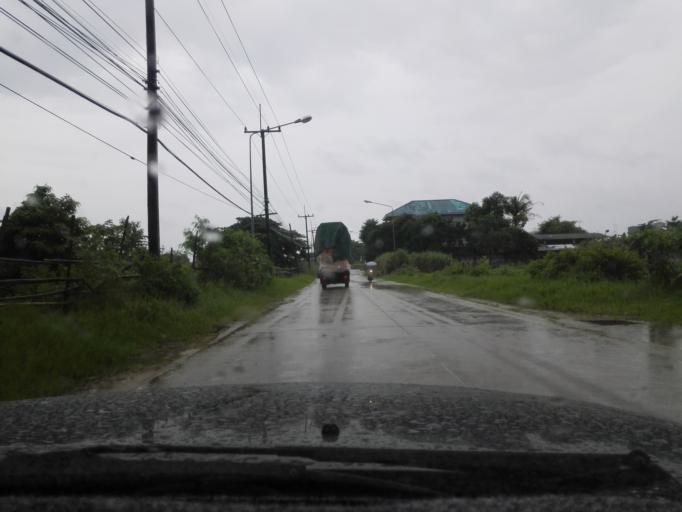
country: TH
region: Tak
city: Mae Sot
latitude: 16.6996
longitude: 98.5732
